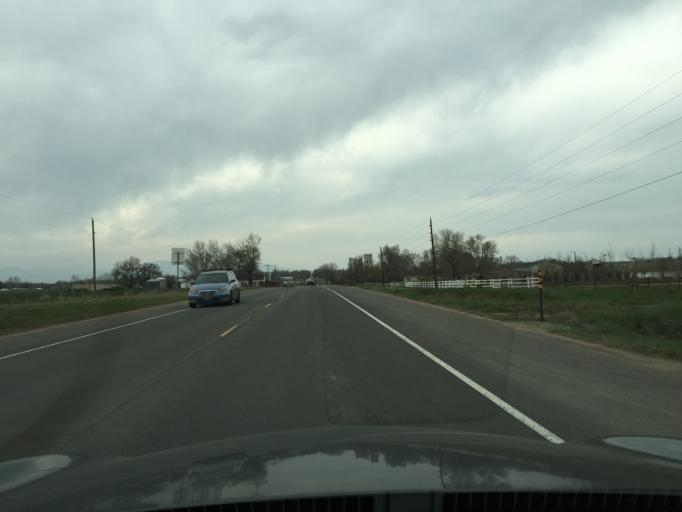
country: US
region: Colorado
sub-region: Boulder County
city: Lafayette
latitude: 40.0003
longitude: -105.0671
